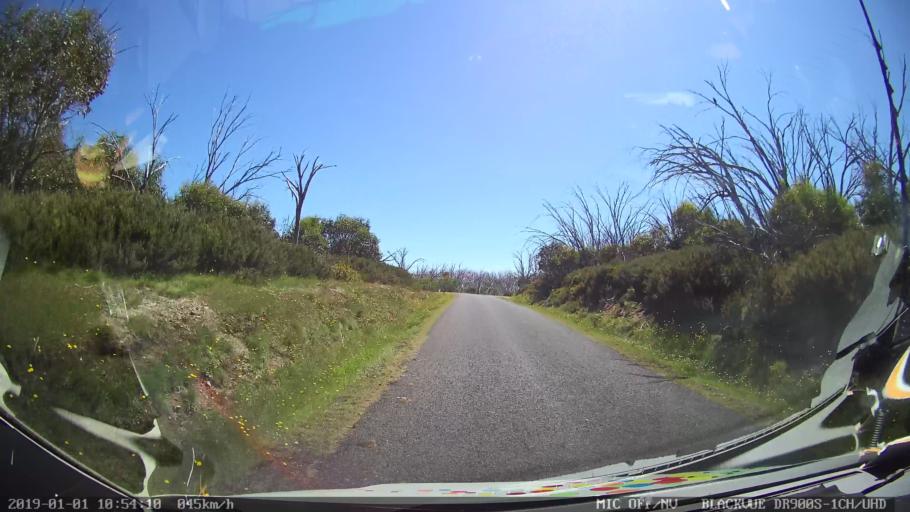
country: AU
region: New South Wales
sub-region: Snowy River
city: Jindabyne
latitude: -36.0102
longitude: 148.3829
